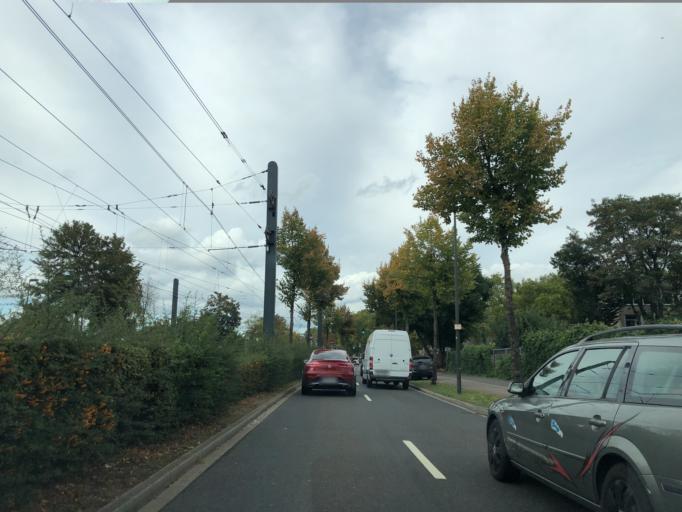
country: DE
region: North Rhine-Westphalia
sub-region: Regierungsbezirk Dusseldorf
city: Dusseldorf
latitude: 51.2023
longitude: 6.8109
